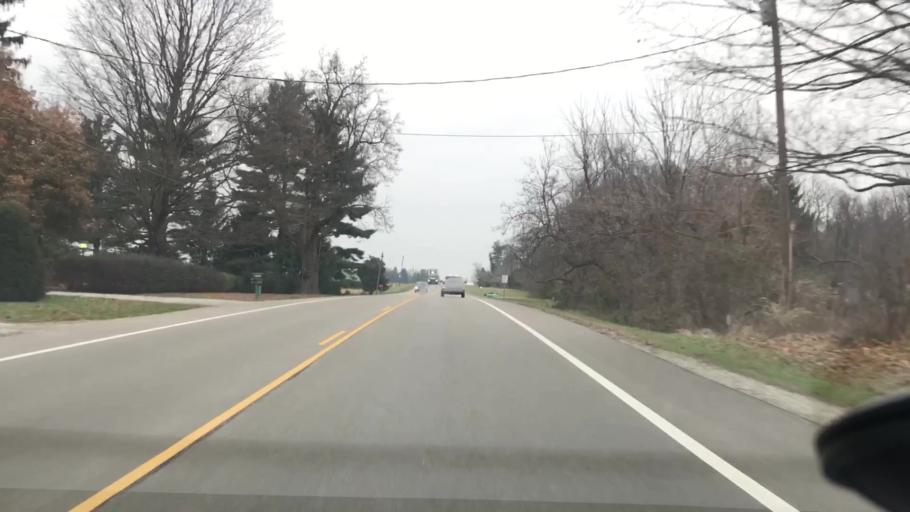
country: US
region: Ohio
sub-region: Greene County
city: Yellow Springs
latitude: 39.8174
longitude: -83.8778
